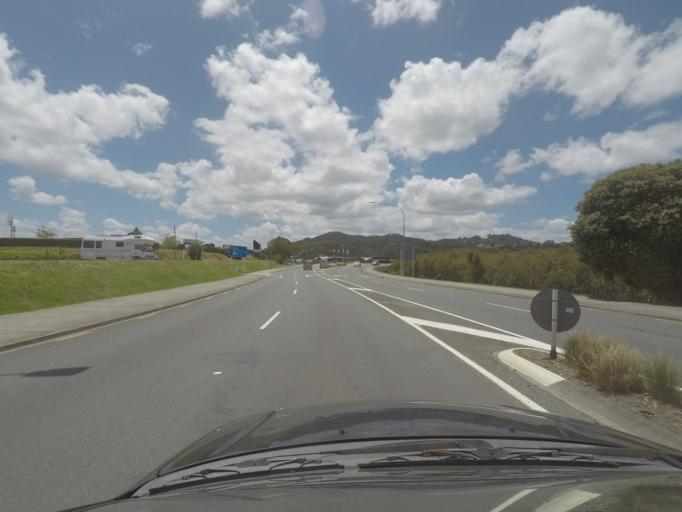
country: NZ
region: Northland
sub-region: Whangarei
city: Whangarei
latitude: -35.7365
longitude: 174.3326
